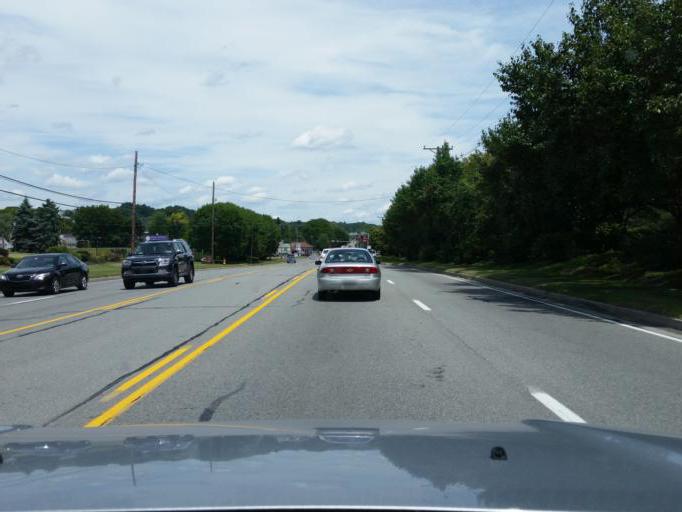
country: US
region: Pennsylvania
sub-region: Blair County
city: Lakemont
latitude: 40.4946
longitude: -78.3954
